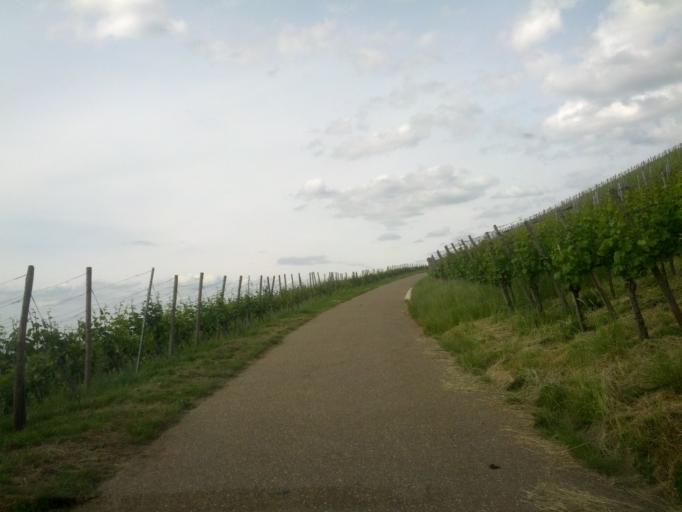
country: DE
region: Baden-Wuerttemberg
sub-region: Freiburg Region
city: Ebringen
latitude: 47.9524
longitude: 7.7796
